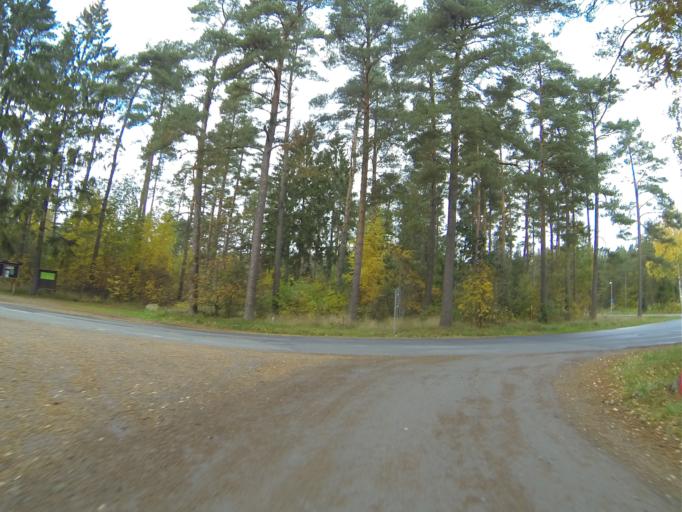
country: SE
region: Skane
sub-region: Sjobo Kommun
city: Sjoebo
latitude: 55.6335
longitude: 13.6555
